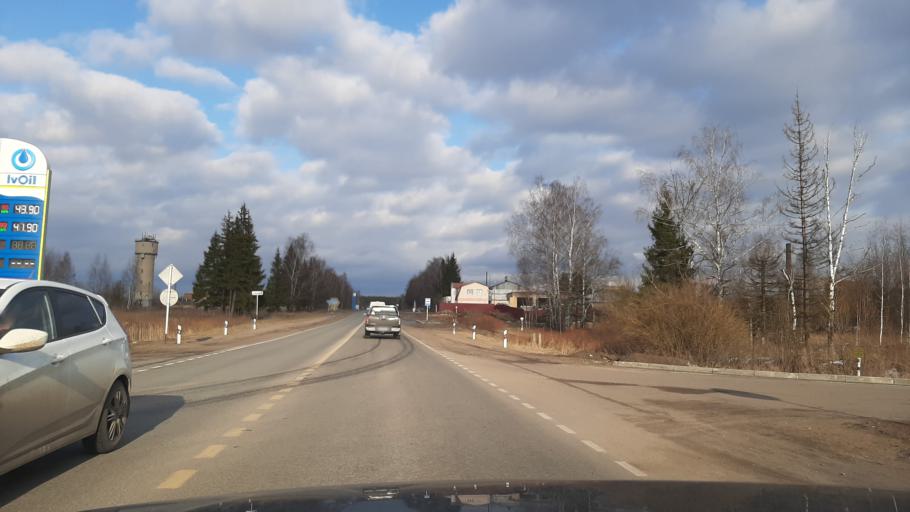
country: RU
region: Ivanovo
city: Teykovo
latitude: 56.8711
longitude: 40.5721
